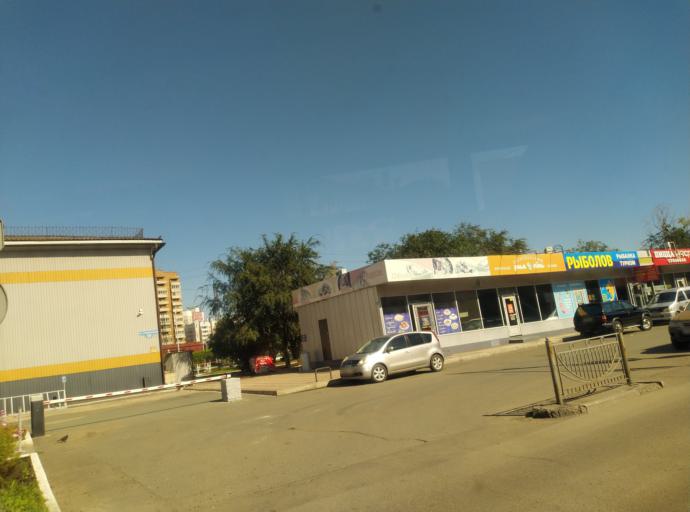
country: RU
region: Krasnoyarskiy
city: Krasnoyarsk
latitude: 55.9790
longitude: 92.8424
